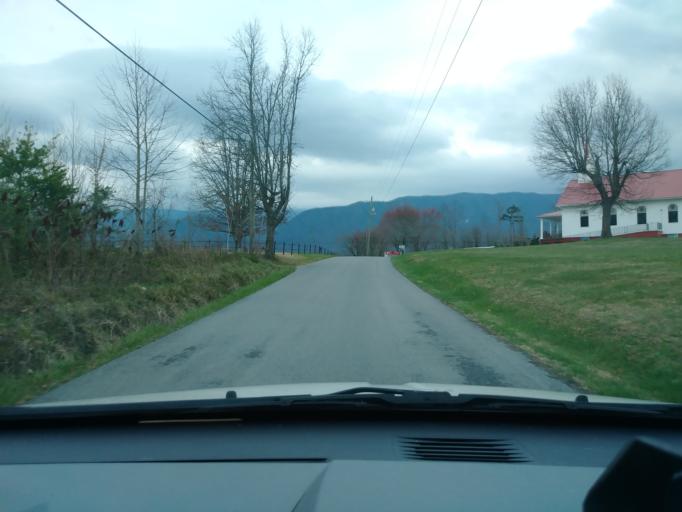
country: US
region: Tennessee
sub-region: Greene County
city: Tusculum
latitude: 36.0891
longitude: -82.7482
